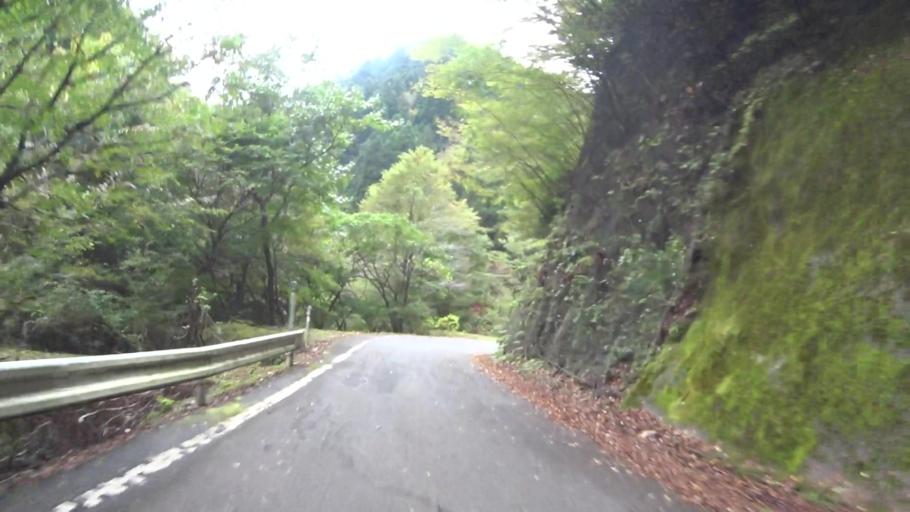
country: JP
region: Fukui
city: Obama
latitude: 35.2763
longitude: 135.7181
